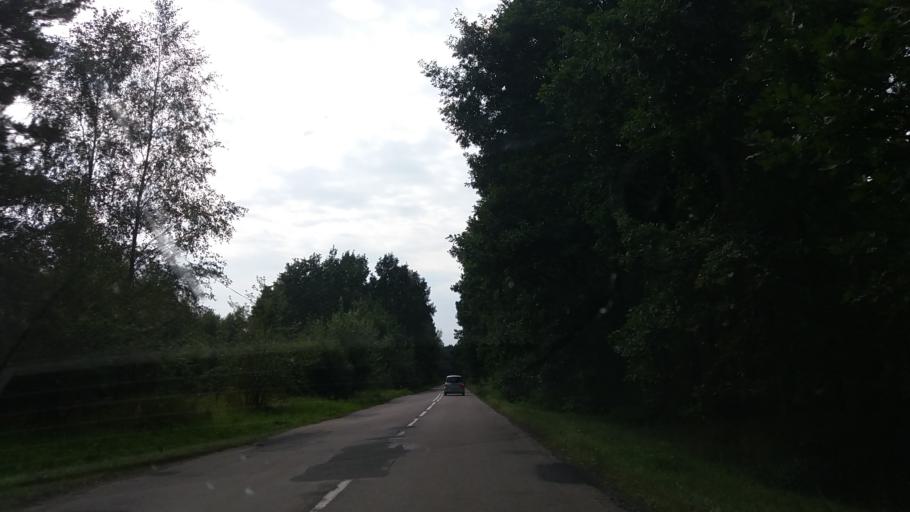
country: PL
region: Lubusz
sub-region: Powiat strzelecko-drezdenecki
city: Zwierzyn
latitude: 52.7304
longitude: 15.6233
